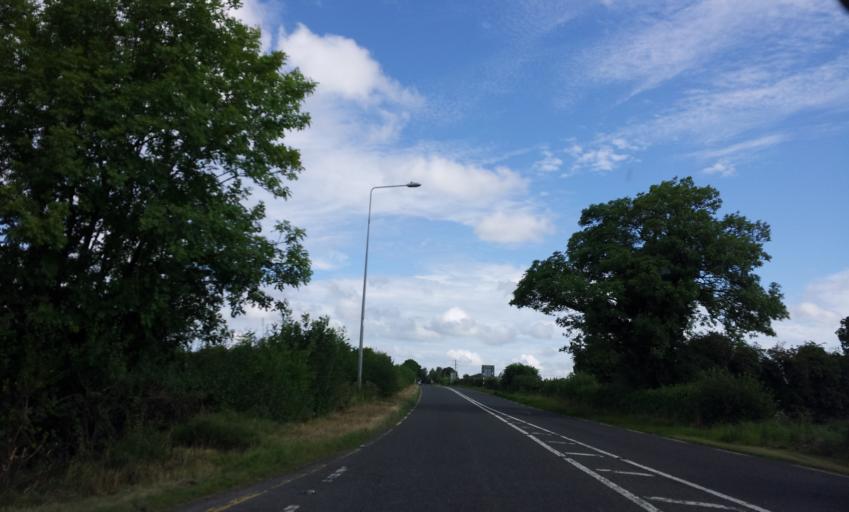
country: IE
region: Leinster
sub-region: Laois
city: Mountrath
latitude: 52.9869
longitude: -7.4895
